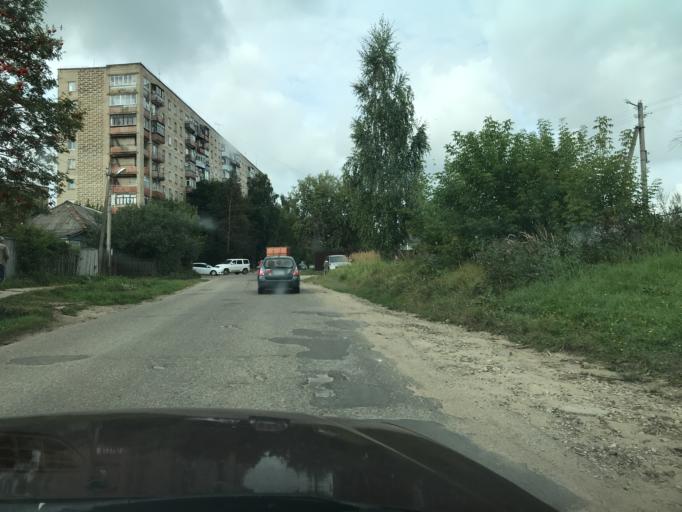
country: RU
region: Kaluga
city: Maloyaroslavets
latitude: 54.9995
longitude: 36.4710
